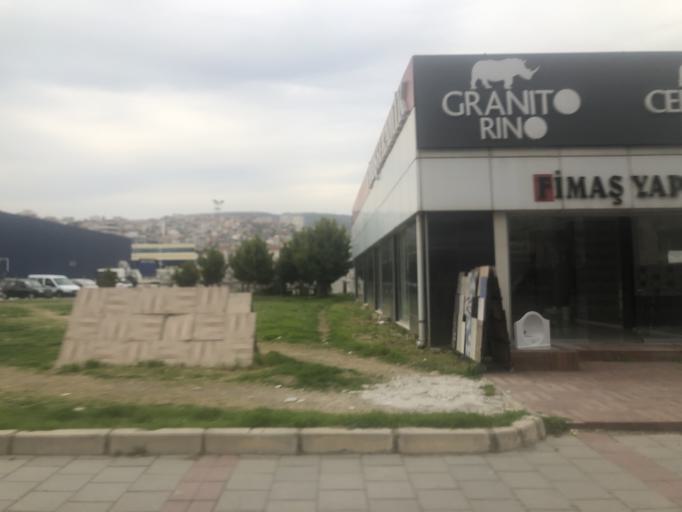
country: TR
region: Izmir
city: Karsiyaka
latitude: 38.4885
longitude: 27.0720
